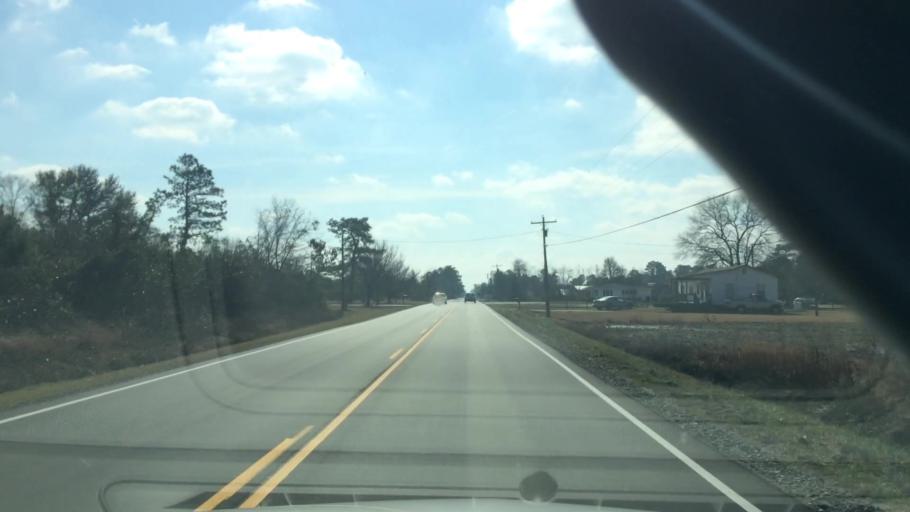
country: US
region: North Carolina
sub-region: Duplin County
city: Beulaville
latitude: 34.9981
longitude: -77.7557
